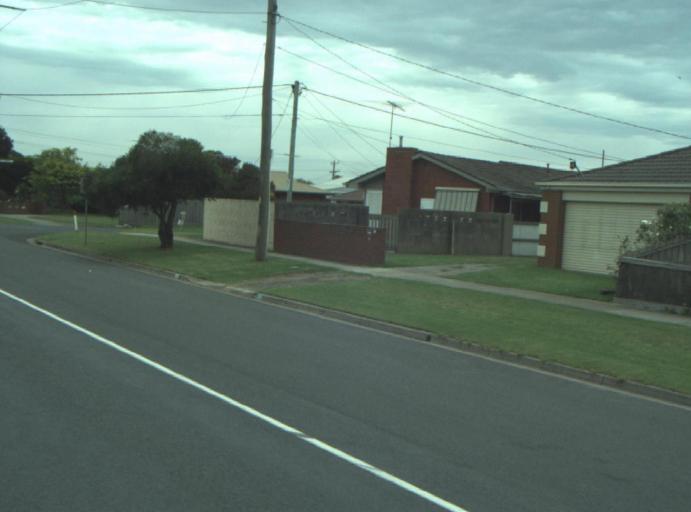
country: AU
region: Victoria
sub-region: Greater Geelong
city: Breakwater
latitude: -38.1834
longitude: 144.3817
